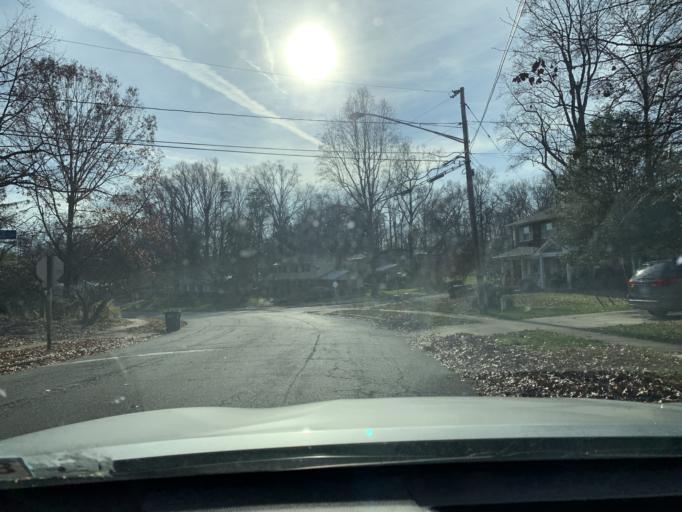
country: US
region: Virginia
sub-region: Fairfax County
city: Jefferson
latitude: 38.8529
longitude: -77.1833
